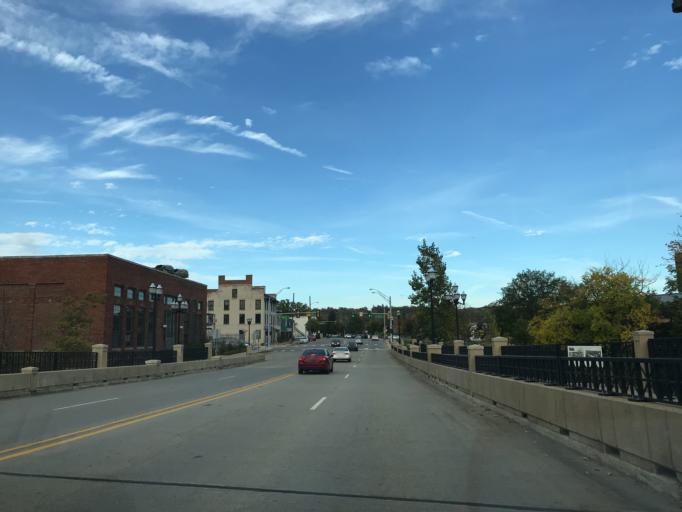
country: US
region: Michigan
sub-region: Washtenaw County
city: Ann Arbor
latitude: 42.2883
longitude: -83.7408
